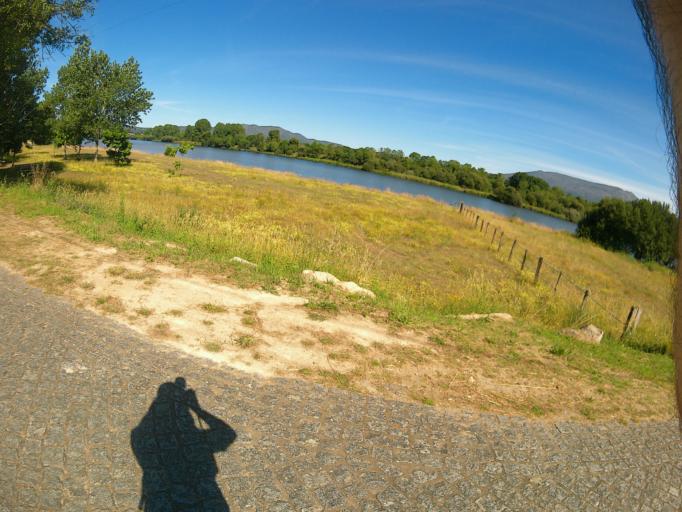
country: PT
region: Viana do Castelo
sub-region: Ponte de Lima
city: Ponte de Lima
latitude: 41.7259
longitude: -8.6720
